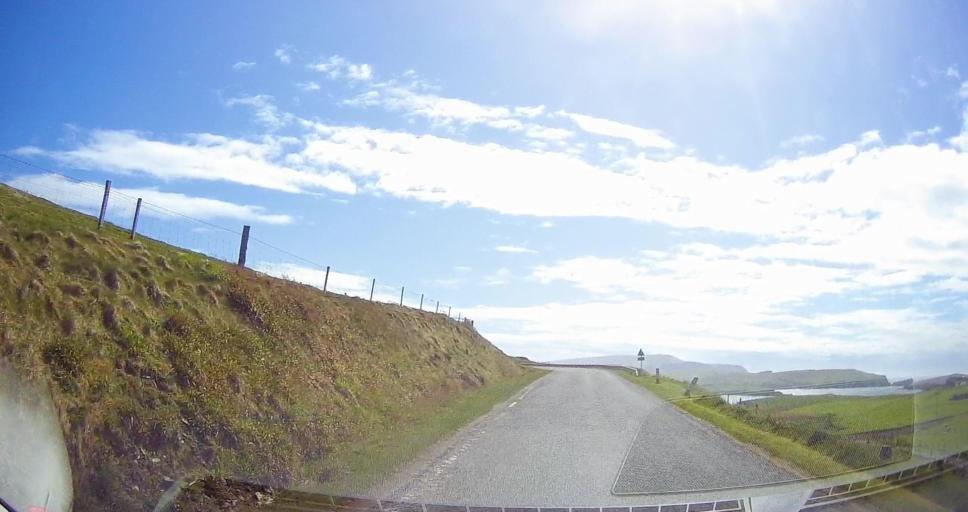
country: GB
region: Scotland
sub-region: Shetland Islands
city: Sandwick
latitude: 59.9605
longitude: -1.3241
